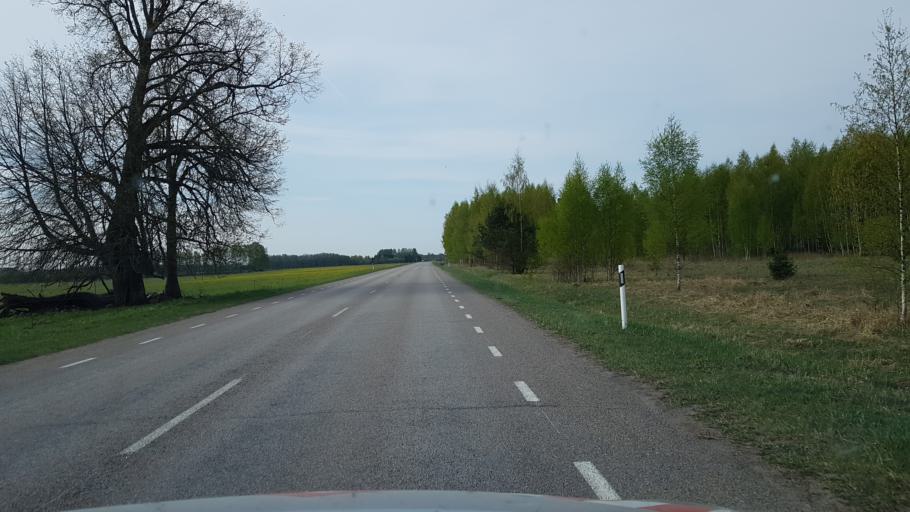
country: EE
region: Paernumaa
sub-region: Audru vald
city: Audru
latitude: 58.3838
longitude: 24.2724
